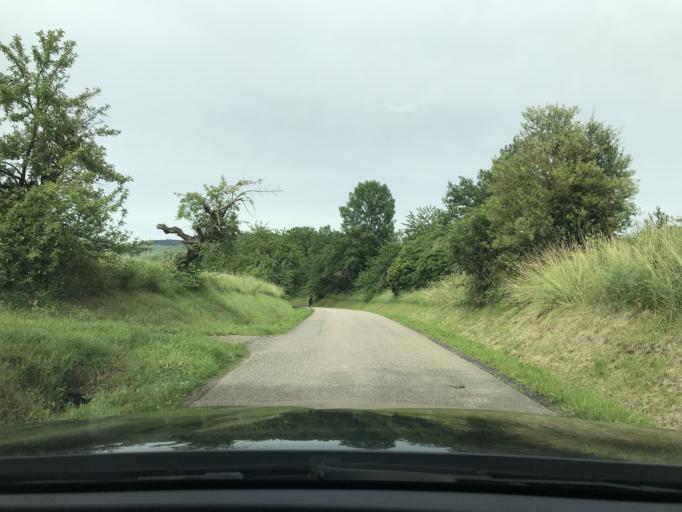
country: DE
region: Baden-Wuerttemberg
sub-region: Regierungsbezirk Stuttgart
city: Weinstadt-Endersbach
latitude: 48.8053
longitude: 9.3623
